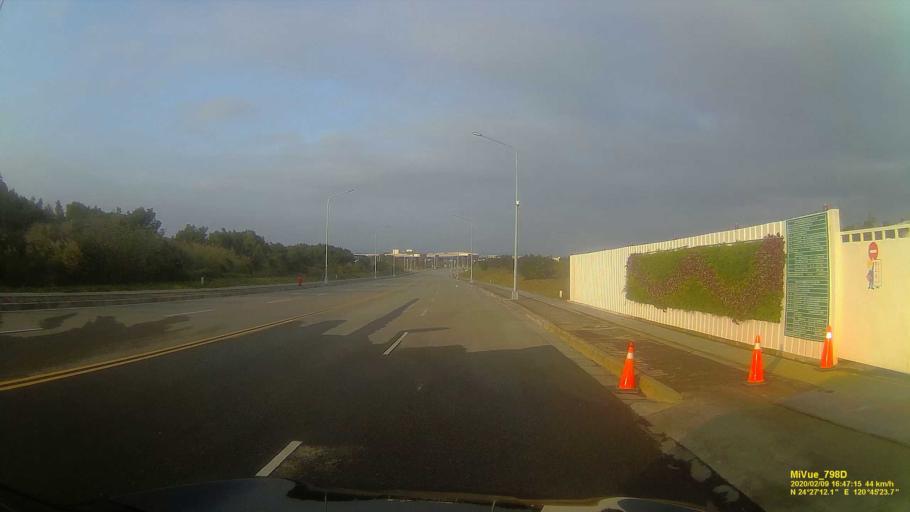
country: TW
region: Taiwan
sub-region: Miaoli
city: Miaoli
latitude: 24.4535
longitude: 120.7566
